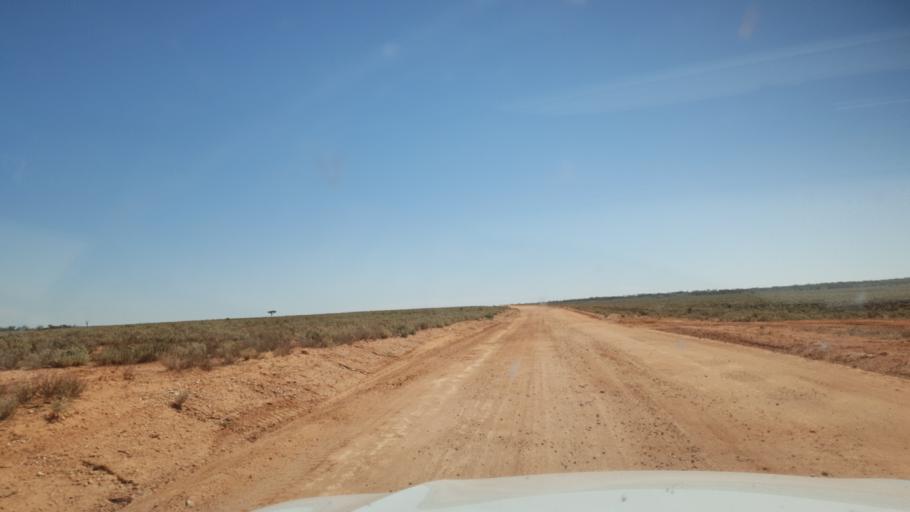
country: AU
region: South Australia
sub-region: Whyalla
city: Whyalla
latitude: -32.6339
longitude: 136.8980
